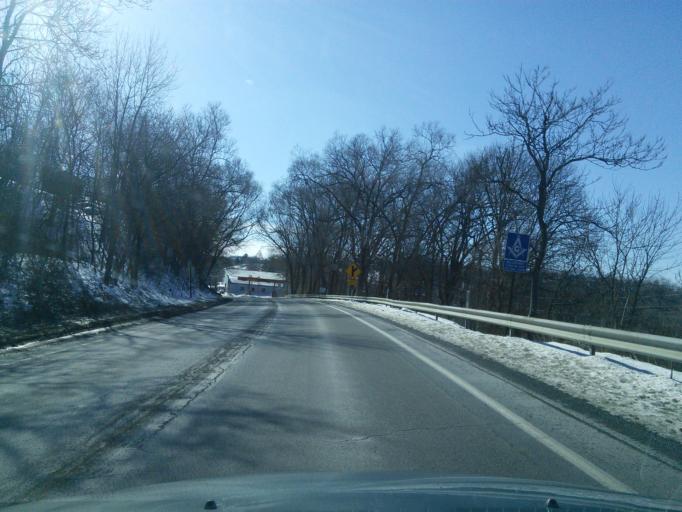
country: US
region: Pennsylvania
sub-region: Centre County
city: Bellefonte
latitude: 40.9186
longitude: -77.7857
